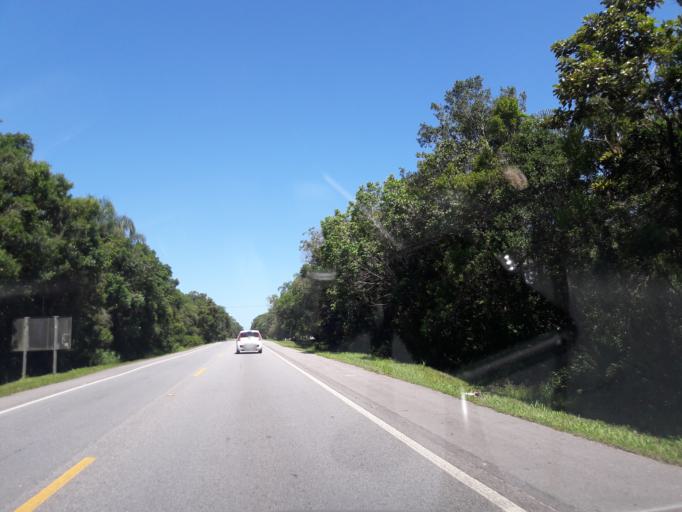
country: BR
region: Parana
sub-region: Pontal Do Parana
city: Pontal do Parana
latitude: -25.6518
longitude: -48.5265
